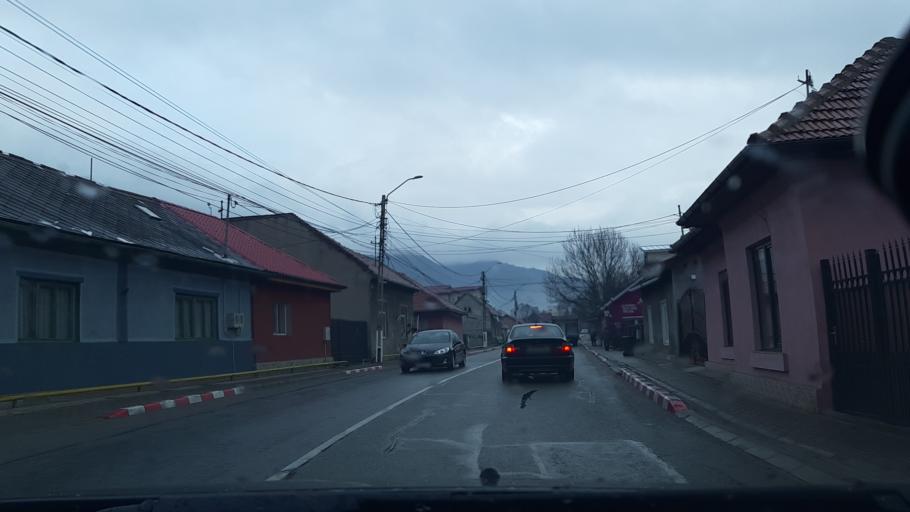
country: RO
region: Hunedoara
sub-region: Municipiul Petrosani
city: Petrosani
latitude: 45.4407
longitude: 23.3705
